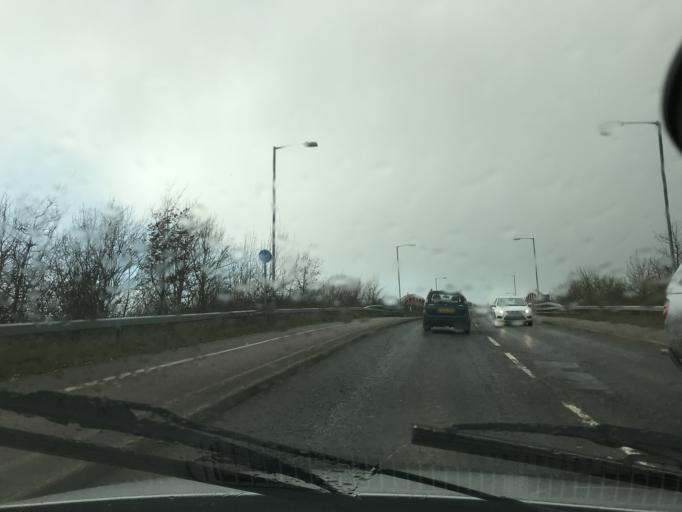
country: GB
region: England
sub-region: Somerset
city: Taunton
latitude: 51.0243
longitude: -3.1330
